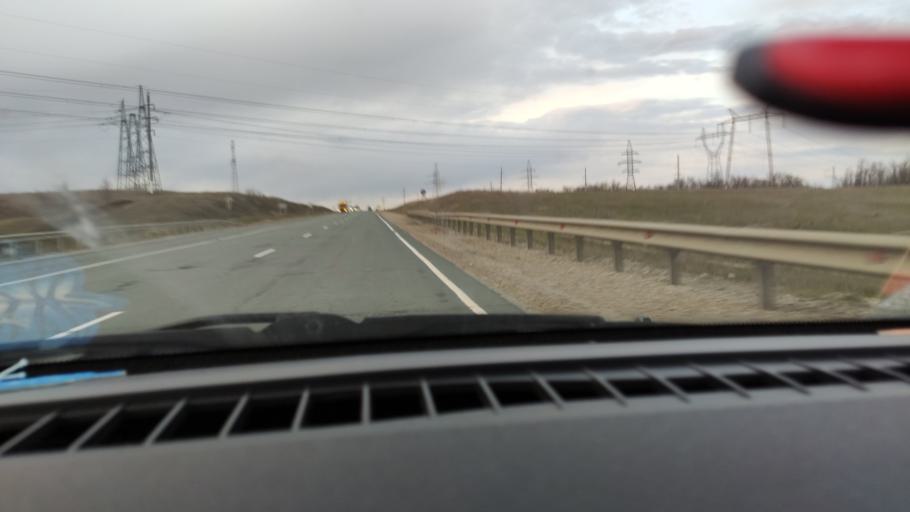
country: RU
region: Saratov
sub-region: Saratovskiy Rayon
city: Saratov
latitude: 51.7686
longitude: 46.0803
